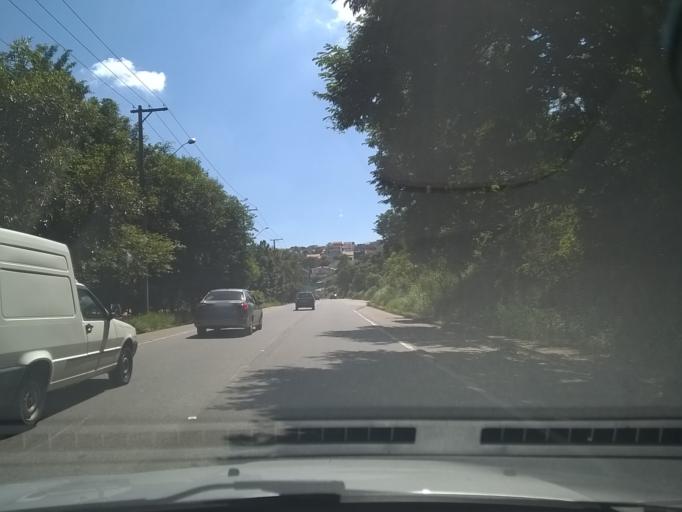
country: BR
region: Sao Paulo
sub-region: Jundiai
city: Jundiai
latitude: -23.2121
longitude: -46.8729
